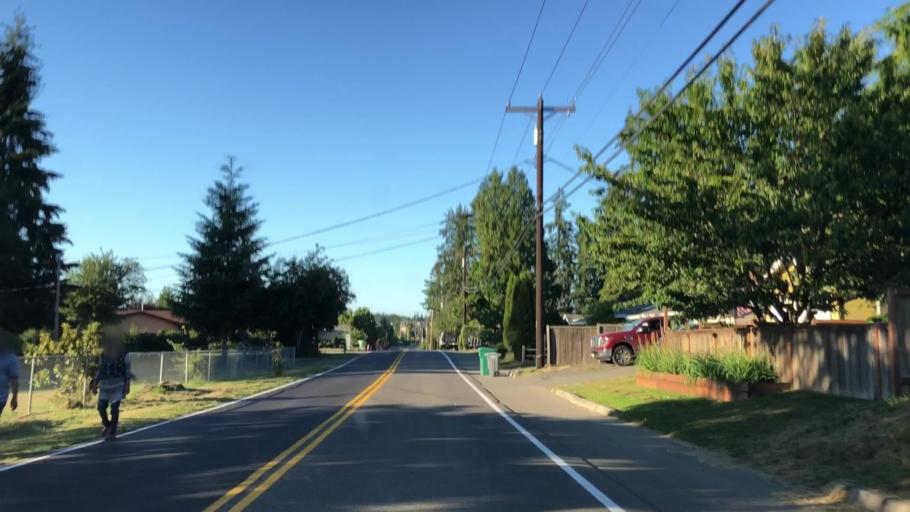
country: US
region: Washington
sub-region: Snohomish County
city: North Creek
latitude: 47.8228
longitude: -122.1898
